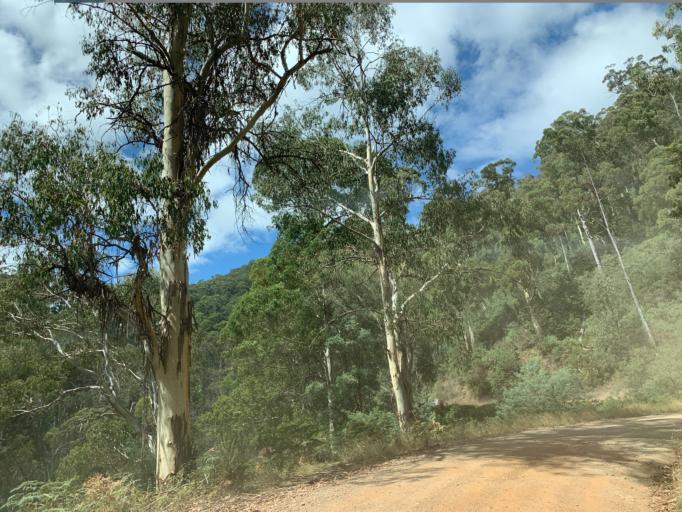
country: AU
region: Victoria
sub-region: Mansfield
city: Mansfield
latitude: -37.0942
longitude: 146.5242
